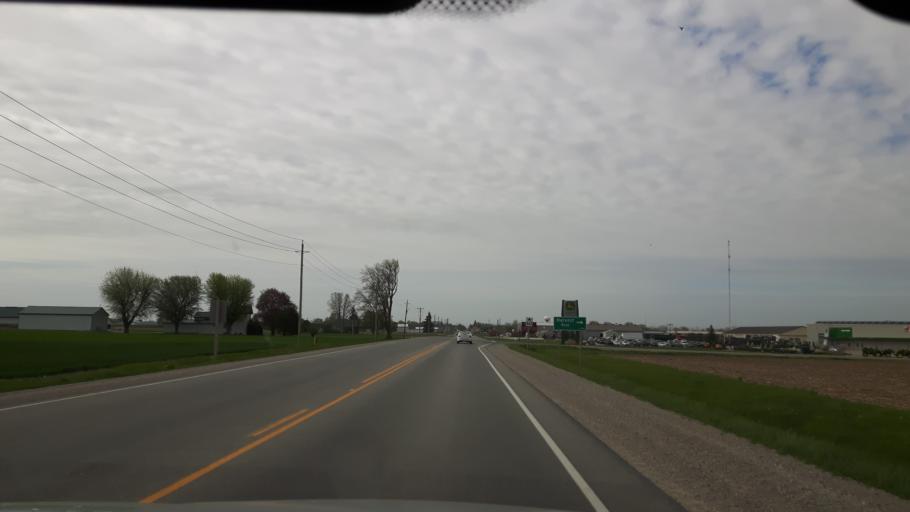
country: CA
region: Ontario
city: South Huron
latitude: 43.3700
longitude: -81.4853
